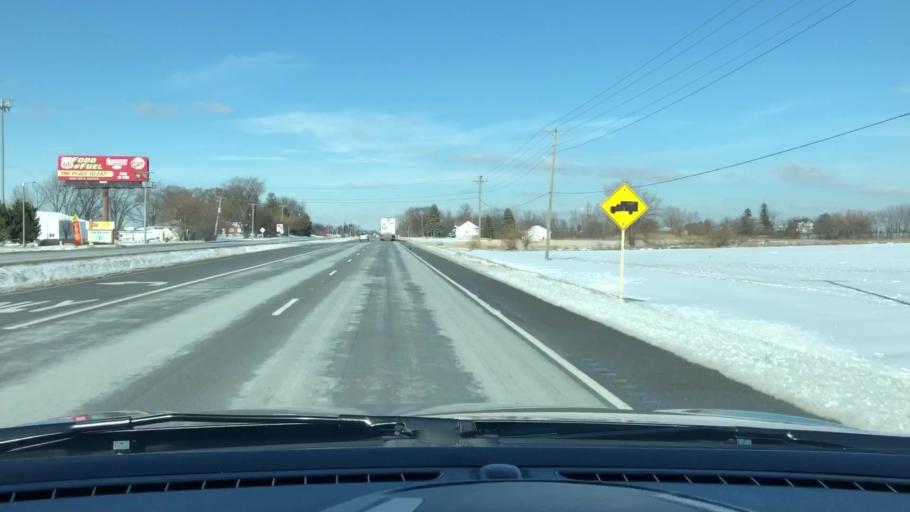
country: US
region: Illinois
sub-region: Will County
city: Preston Heights
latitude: 41.4725
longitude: -88.0798
